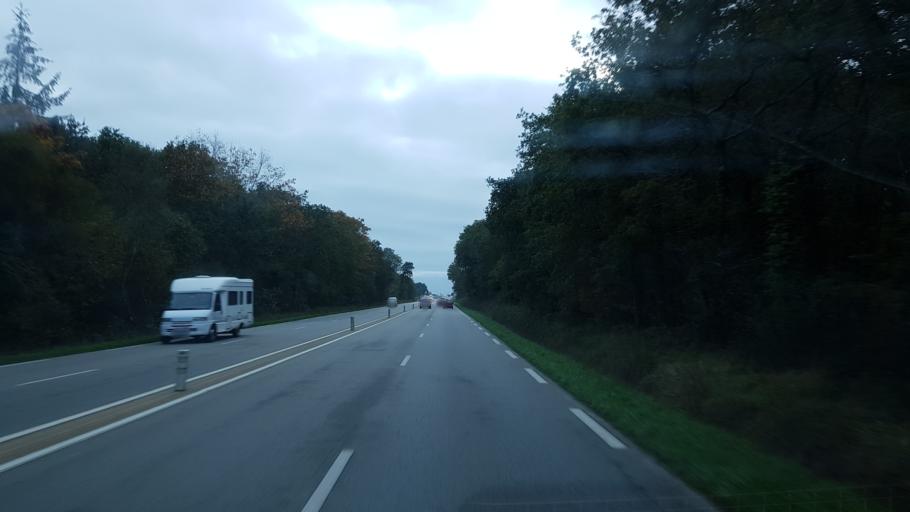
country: FR
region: Brittany
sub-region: Departement du Morbihan
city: Sarzeau
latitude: 47.5320
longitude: -2.7479
